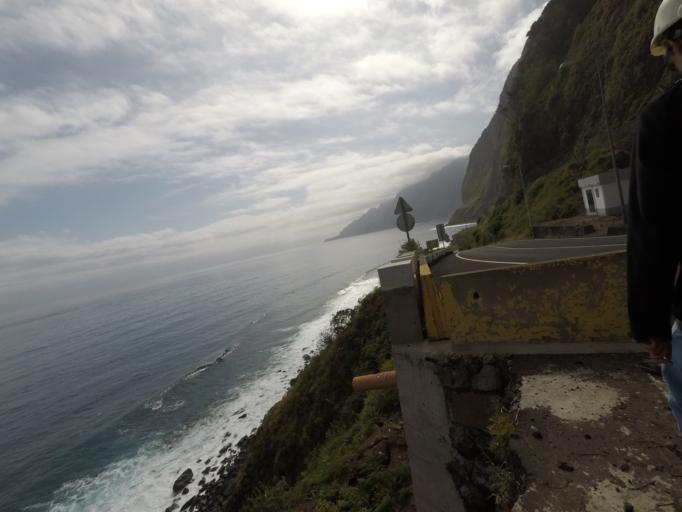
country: PT
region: Madeira
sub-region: Sao Vicente
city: Sao Vicente
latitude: 32.8158
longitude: -17.0833
